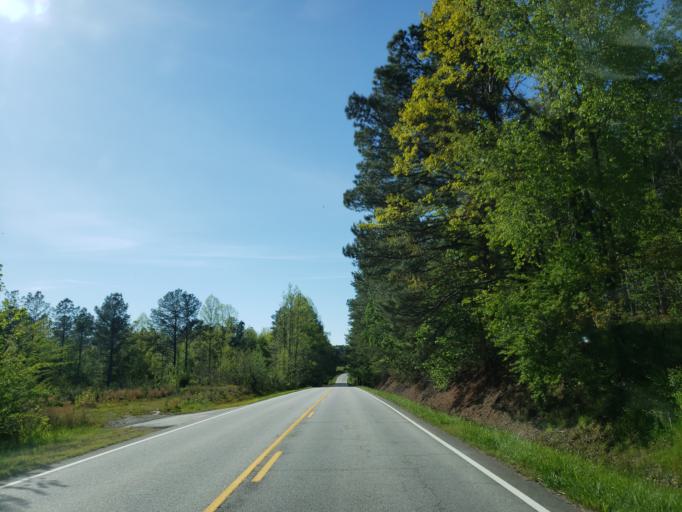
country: US
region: Georgia
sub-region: Haralson County
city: Tallapoosa
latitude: 33.8764
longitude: -85.3044
